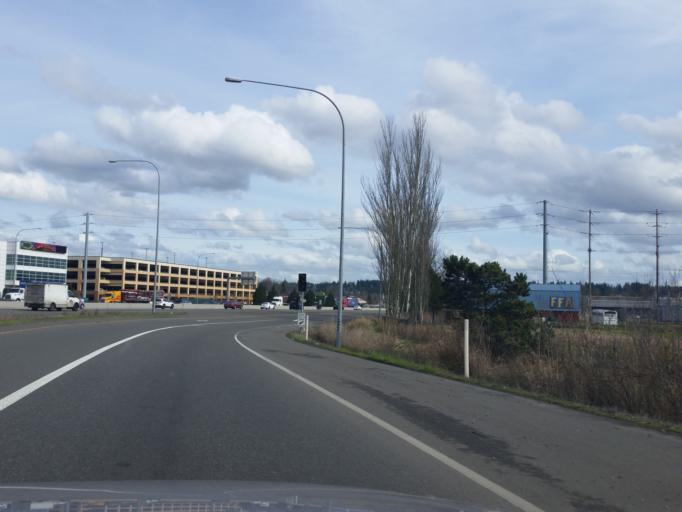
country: US
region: Washington
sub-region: Pierce County
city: Fife
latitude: 47.2404
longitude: -122.3541
